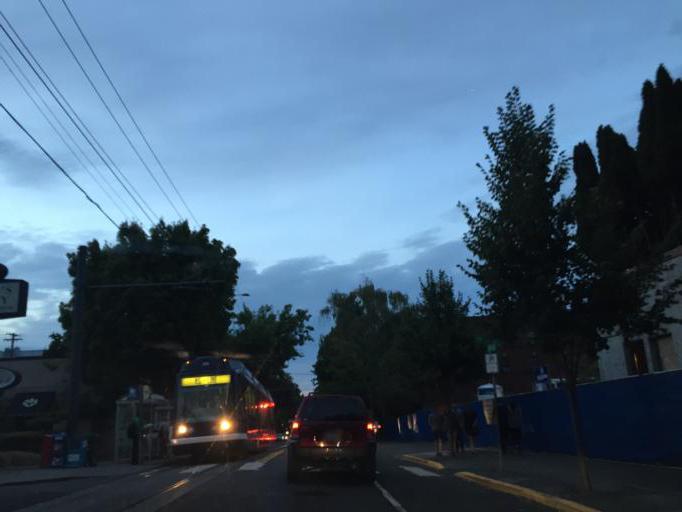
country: US
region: Oregon
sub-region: Multnomah County
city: Portland
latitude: 45.5303
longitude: -122.6986
